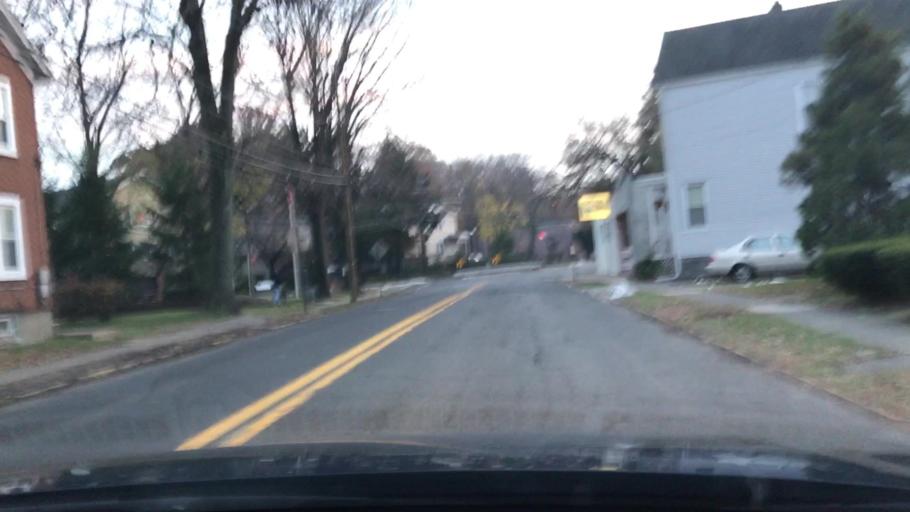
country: US
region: New Jersey
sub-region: Bergen County
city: Wallington
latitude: 40.8447
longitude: -74.1131
